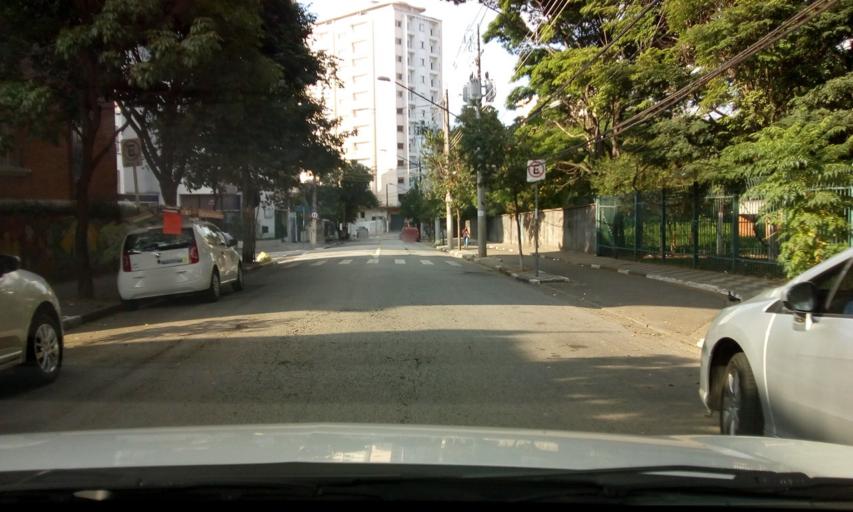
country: BR
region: Sao Paulo
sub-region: Sao Paulo
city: Sao Paulo
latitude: -23.5649
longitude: -46.6307
